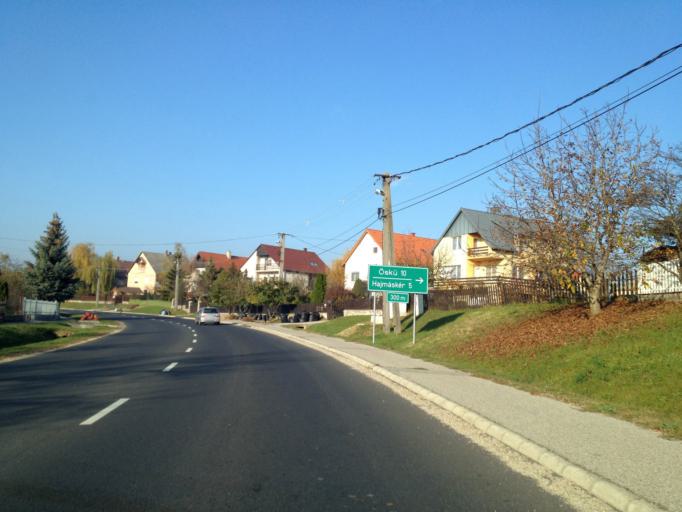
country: HU
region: Veszprem
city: Veszprem
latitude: 47.1413
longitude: 17.9513
